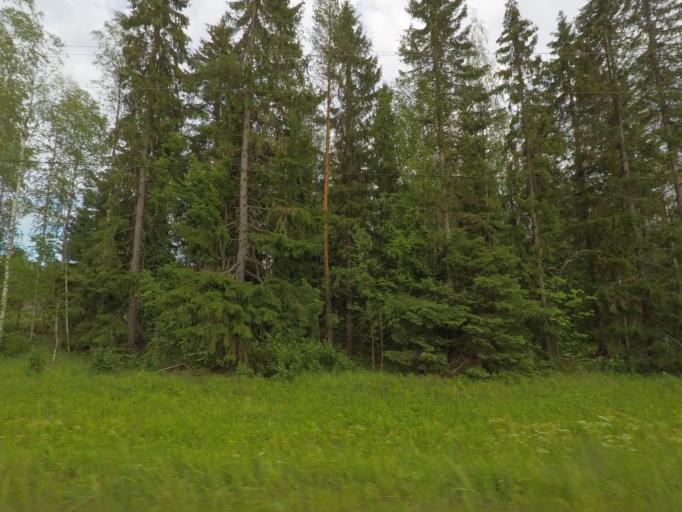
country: FI
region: Paijanne Tavastia
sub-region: Lahti
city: Hollola
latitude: 60.8922
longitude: 25.5188
